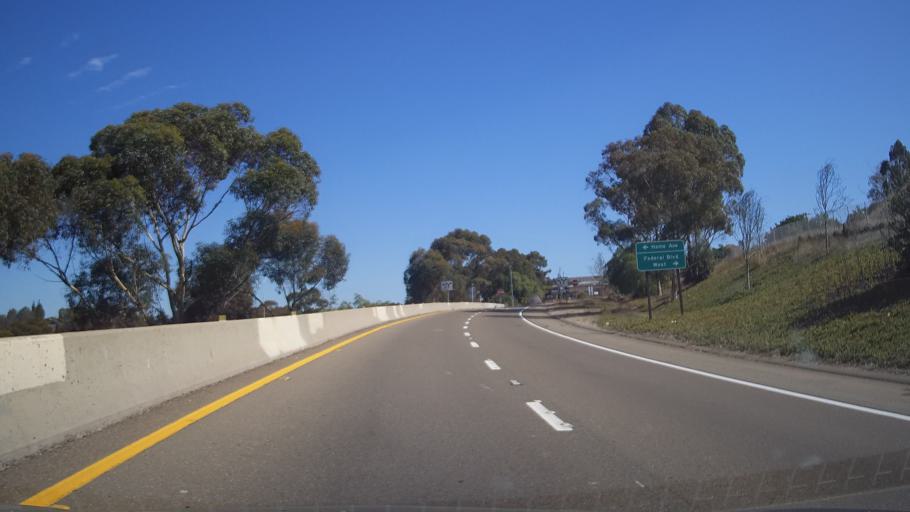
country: US
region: California
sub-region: San Diego County
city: National City
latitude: 32.7174
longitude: -117.1119
